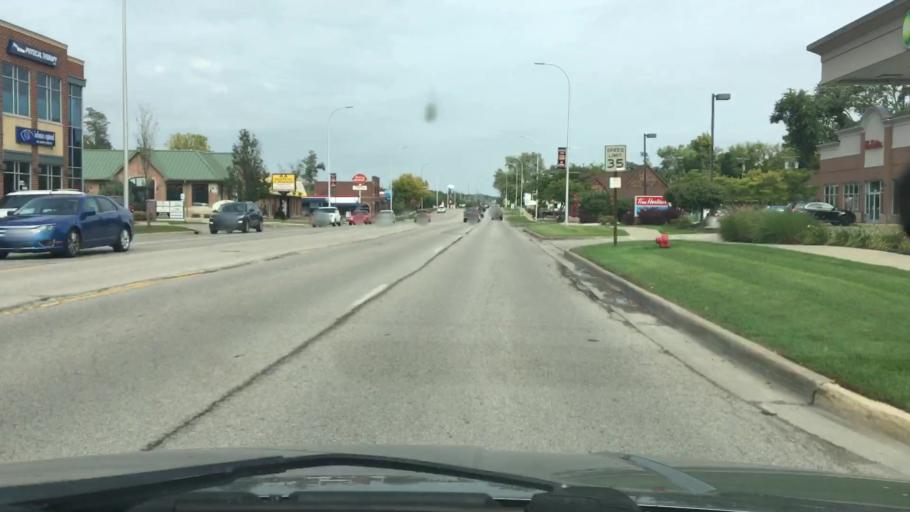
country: US
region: Michigan
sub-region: Livingston County
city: Brighton
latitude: 42.5305
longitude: -83.7808
